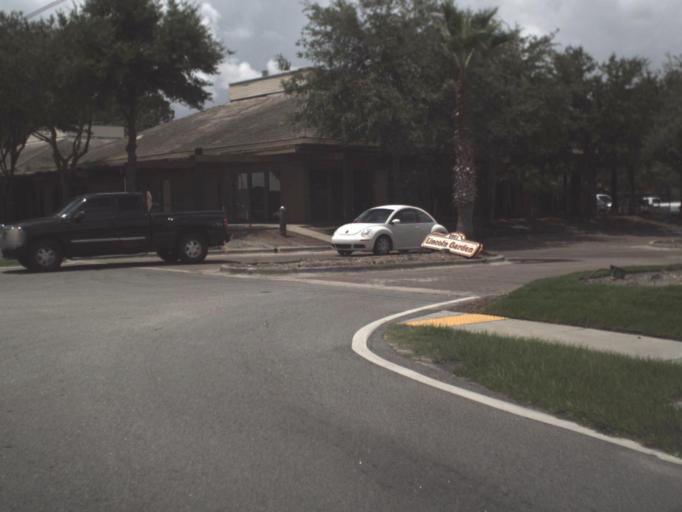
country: US
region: Florida
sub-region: Hillsborough County
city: Carrollwood
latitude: 28.0360
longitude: -82.4913
